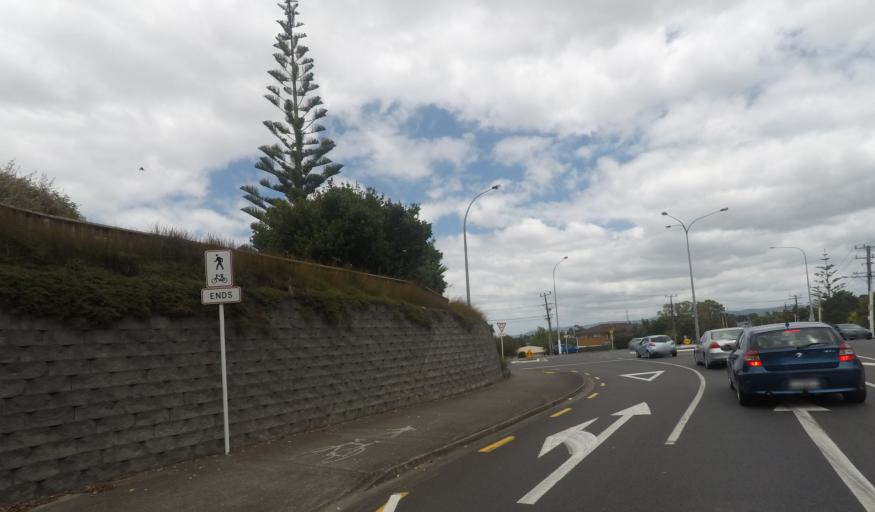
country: NZ
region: Auckland
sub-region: Auckland
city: Rosebank
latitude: -36.8308
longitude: 174.6062
